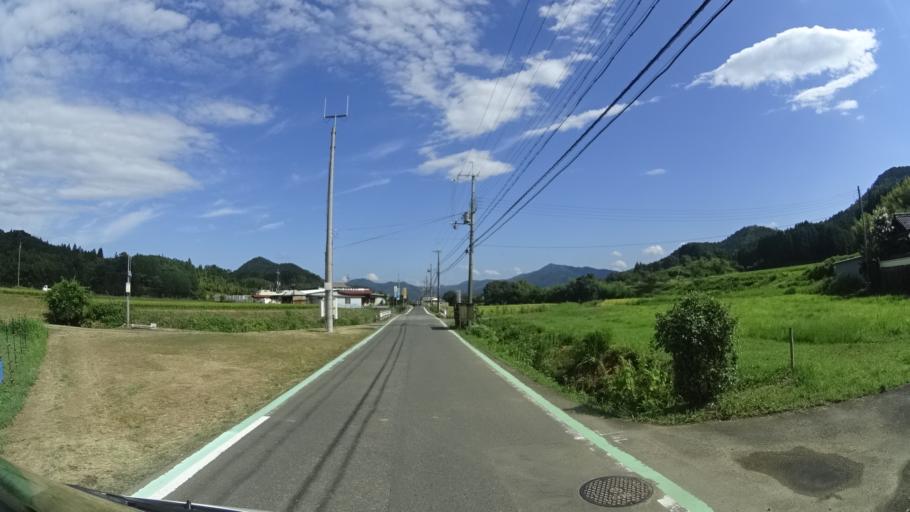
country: JP
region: Kyoto
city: Fukuchiyama
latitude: 35.3241
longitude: 135.1779
